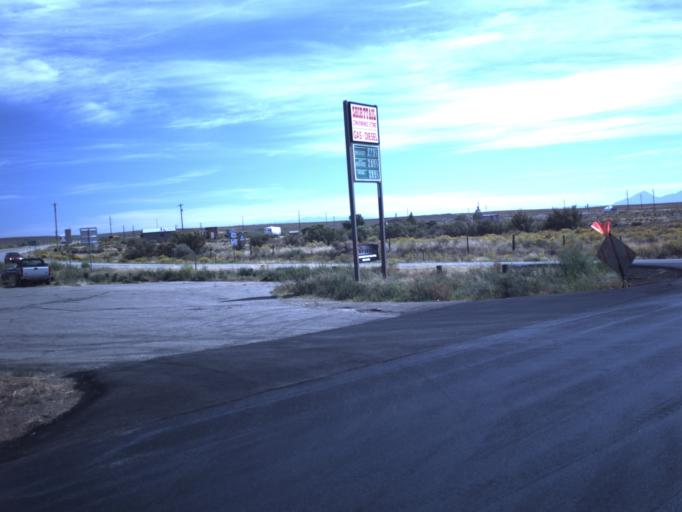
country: US
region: Utah
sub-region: San Juan County
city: Blanding
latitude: 37.5731
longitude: -109.4878
